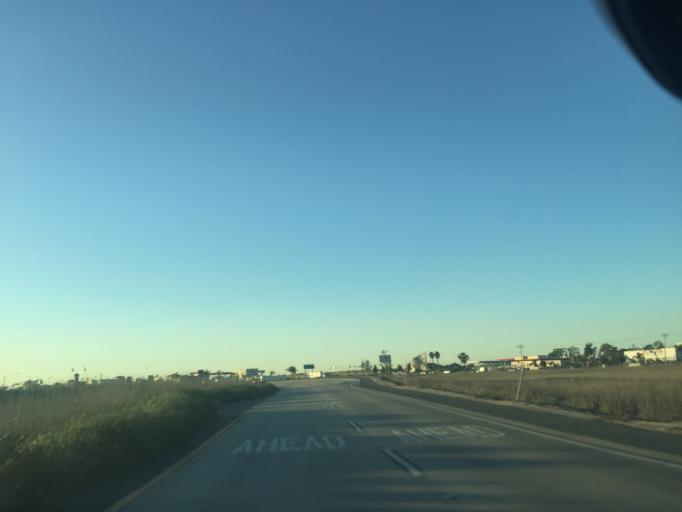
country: MX
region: Baja California
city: Tijuana
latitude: 32.5652
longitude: -116.9593
